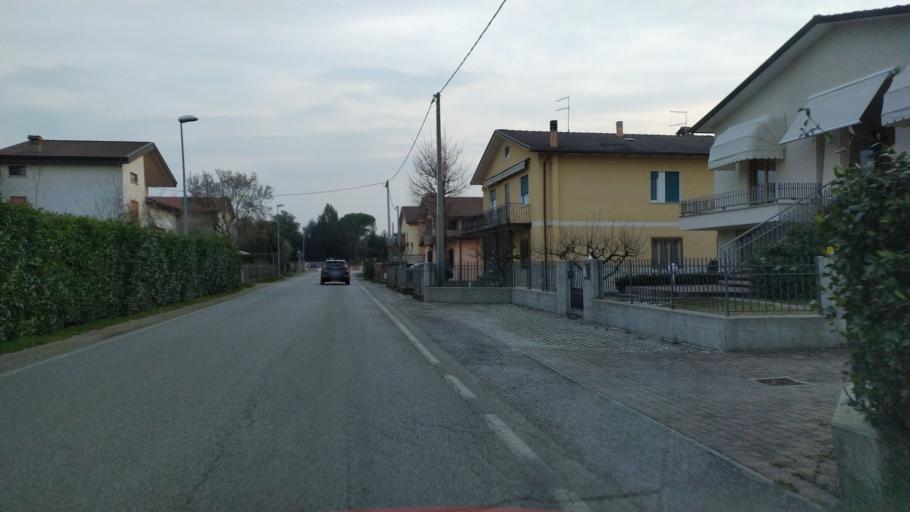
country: IT
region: Veneto
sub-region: Provincia di Vicenza
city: Montecchio Precalcino
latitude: 45.6538
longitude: 11.5576
